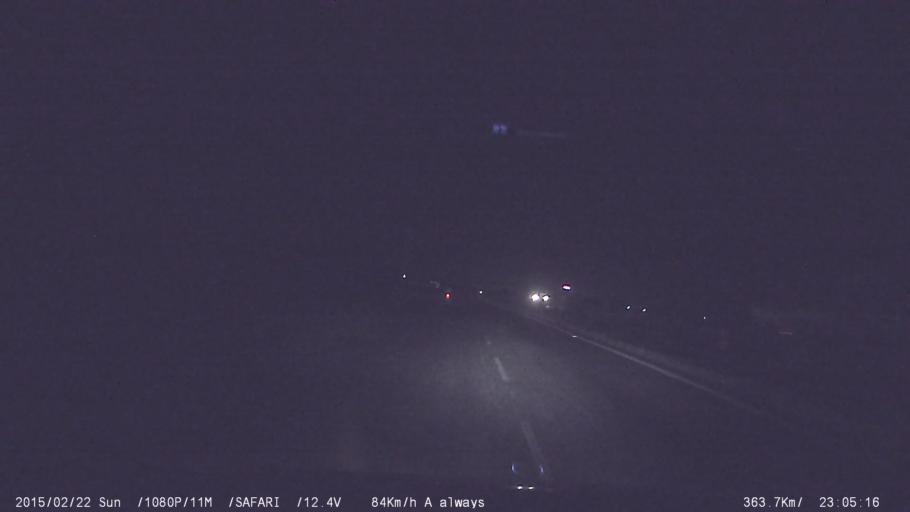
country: IN
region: Tamil Nadu
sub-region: Namakkal
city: Rasipuram
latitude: 11.4131
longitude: 78.1585
